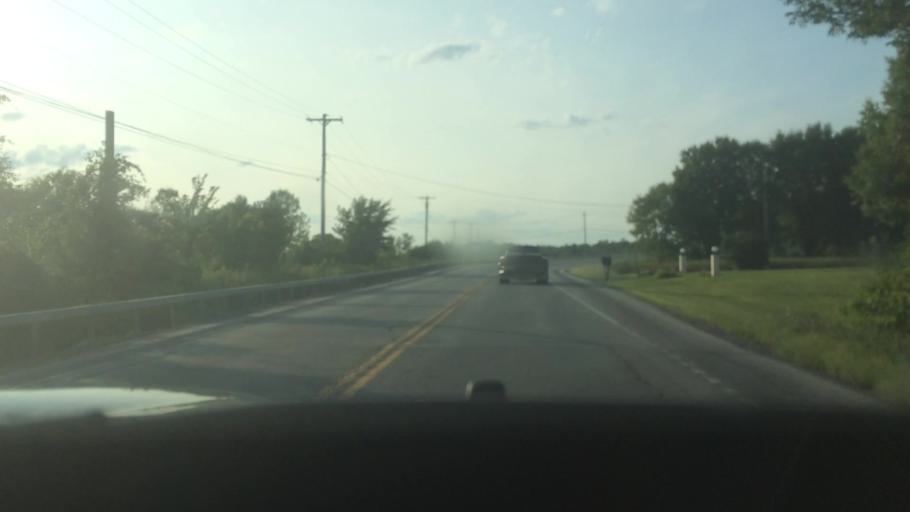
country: US
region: New York
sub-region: St. Lawrence County
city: Ogdensburg
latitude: 44.6814
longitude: -75.4442
